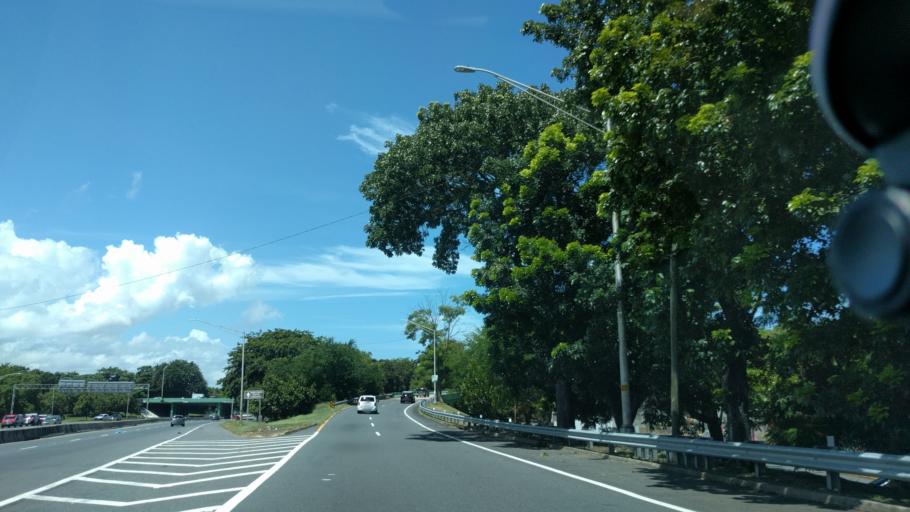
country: PR
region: San Juan
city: San Juan
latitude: 18.4404
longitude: -66.0678
